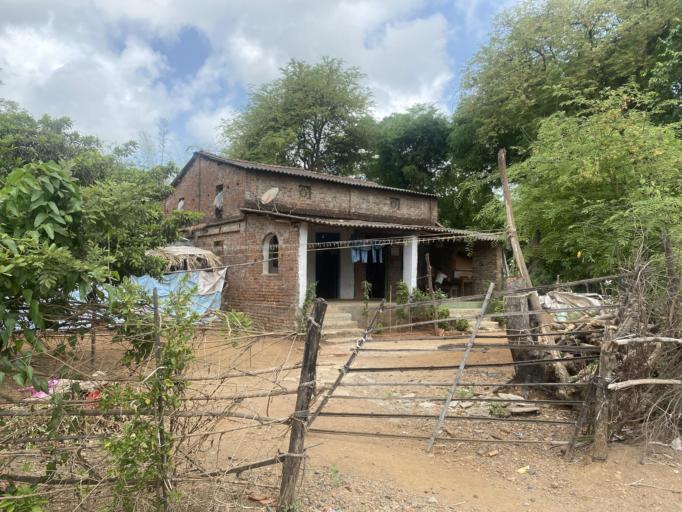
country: IN
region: Gujarat
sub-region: Valsad
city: Vapi
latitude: 20.3180
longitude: 72.8360
